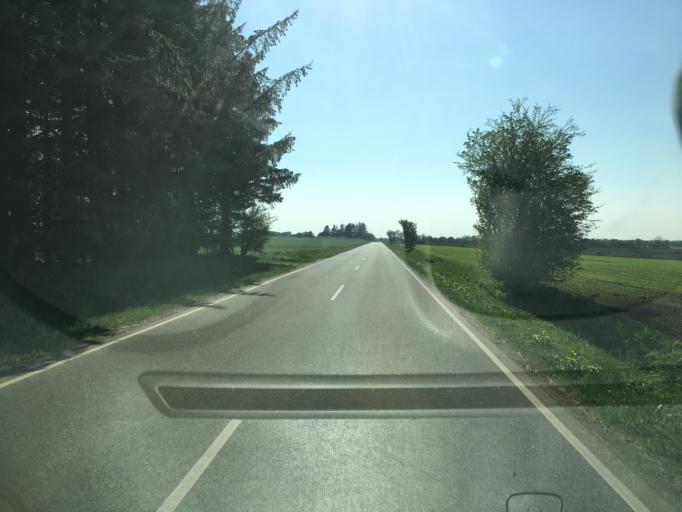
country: DK
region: South Denmark
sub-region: Haderslev Kommune
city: Vojens
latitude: 55.3086
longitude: 9.2764
